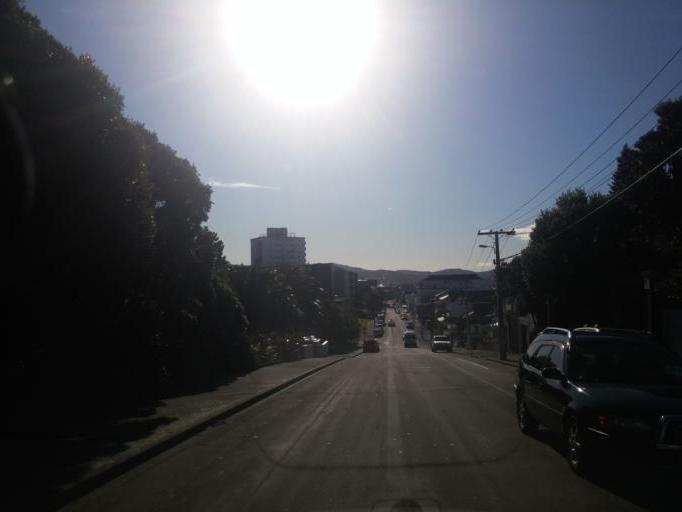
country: NZ
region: Wellington
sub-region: Wellington City
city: Wellington
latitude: -41.3100
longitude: 174.7759
